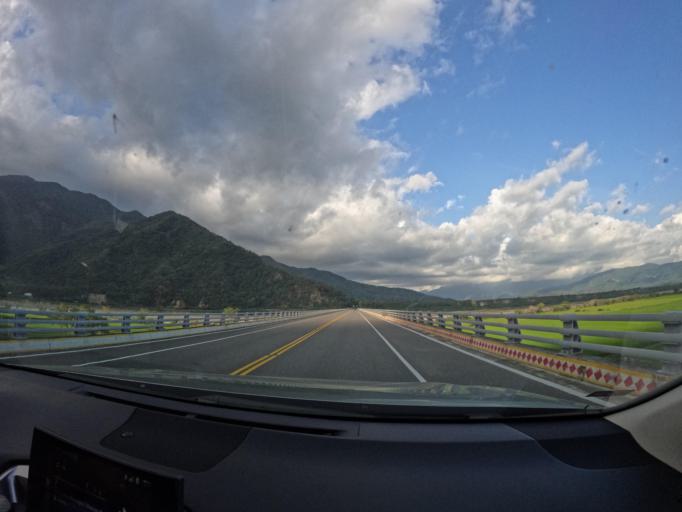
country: TW
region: Taiwan
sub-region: Taitung
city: Taitung
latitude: 23.1232
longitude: 121.1665
